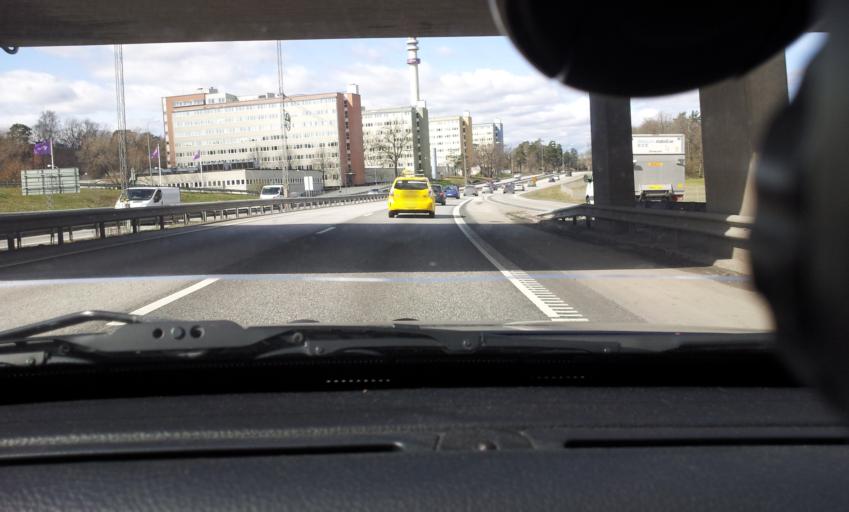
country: SE
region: Stockholm
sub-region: Stockholms Kommun
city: Arsta
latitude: 59.2441
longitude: 18.1070
